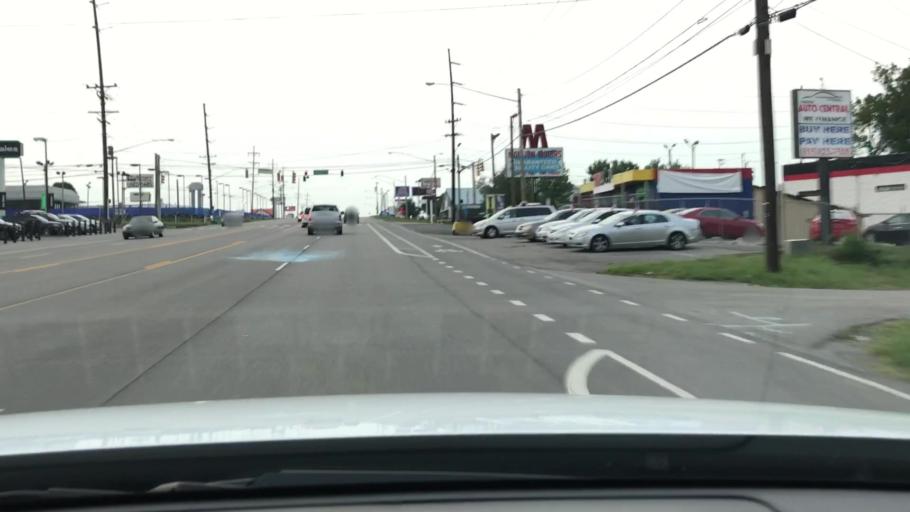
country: US
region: Tennessee
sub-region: Davidson County
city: Goodlettsville
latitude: 36.2860
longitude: -86.7057
